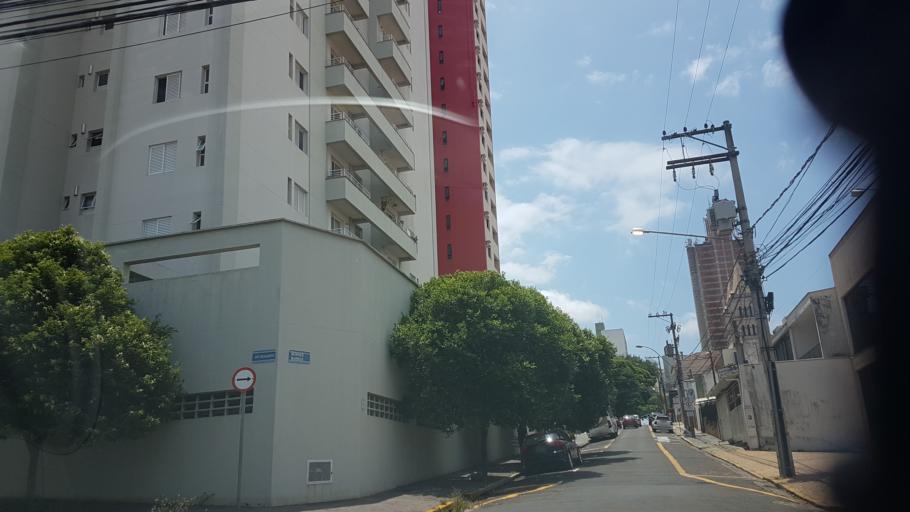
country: BR
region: Sao Paulo
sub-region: Piracicaba
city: Piracicaba
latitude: -22.7243
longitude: -47.6514
